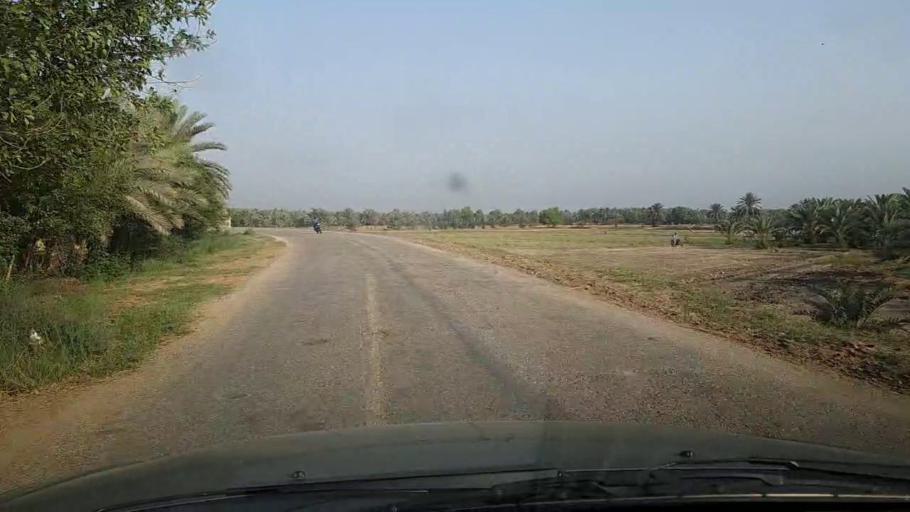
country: PK
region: Sindh
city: Pir jo Goth
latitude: 27.5627
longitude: 68.6585
